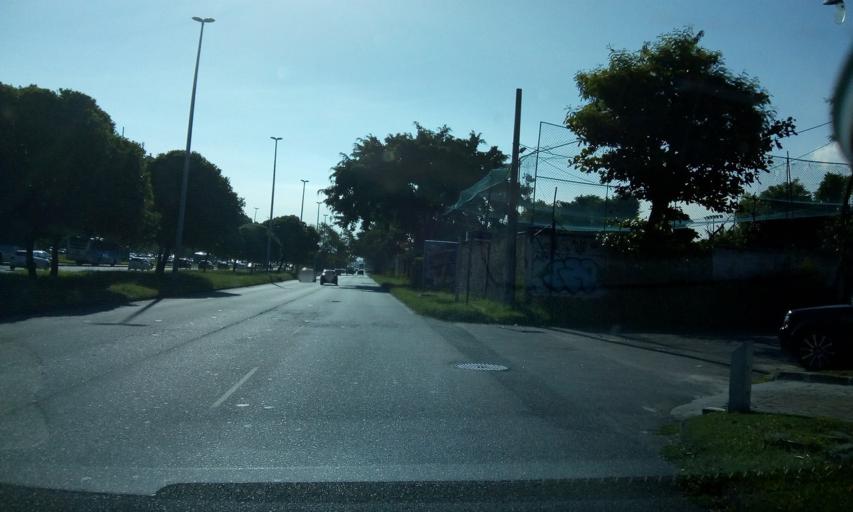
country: BR
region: Rio de Janeiro
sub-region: Nilopolis
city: Nilopolis
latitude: -23.0001
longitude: -43.3903
